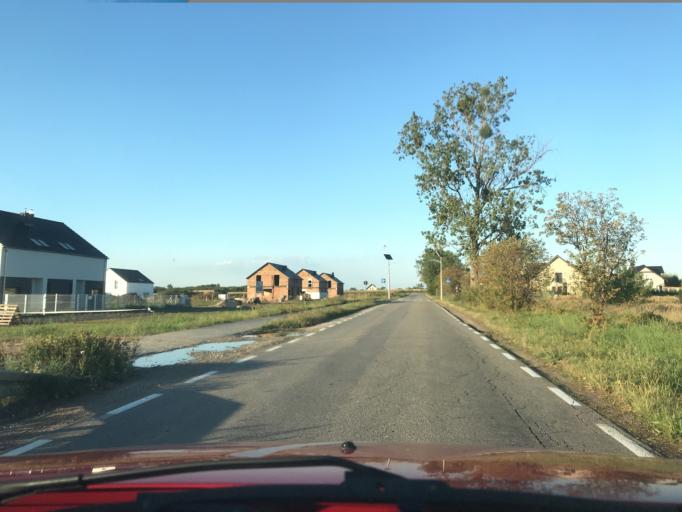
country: PL
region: Greater Poland Voivodeship
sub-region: Powiat poznanski
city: Tarnowo Podgorne
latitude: 52.4385
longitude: 16.7093
